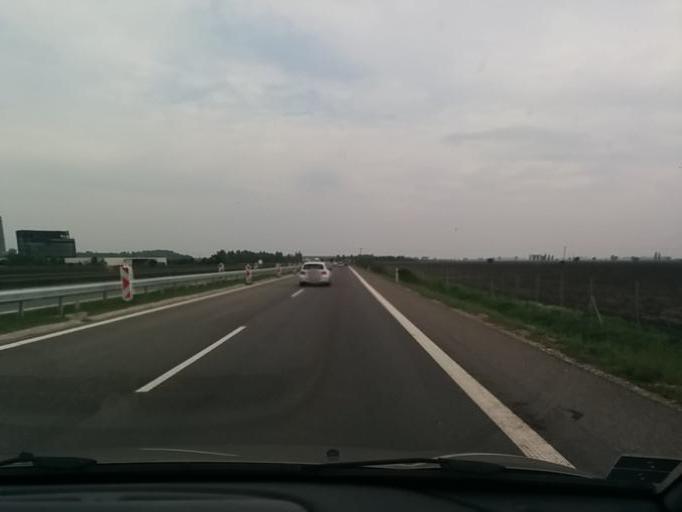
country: SK
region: Trnavsky
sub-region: Okres Galanta
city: Galanta
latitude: 48.2768
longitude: 17.7146
